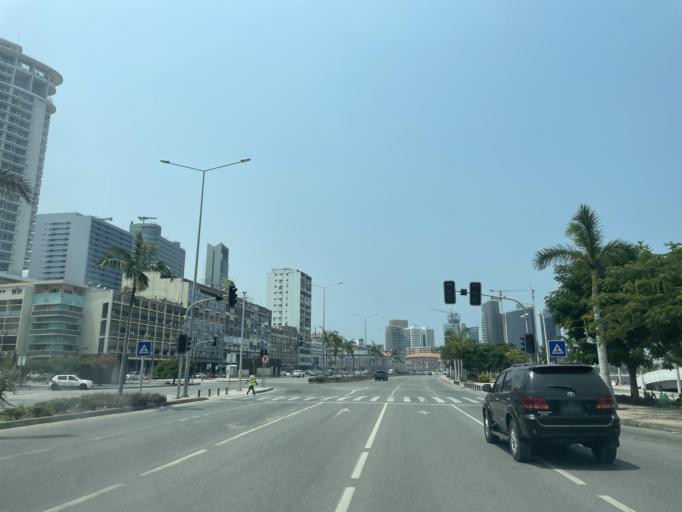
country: AO
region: Luanda
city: Luanda
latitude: -8.8066
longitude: 13.2390
